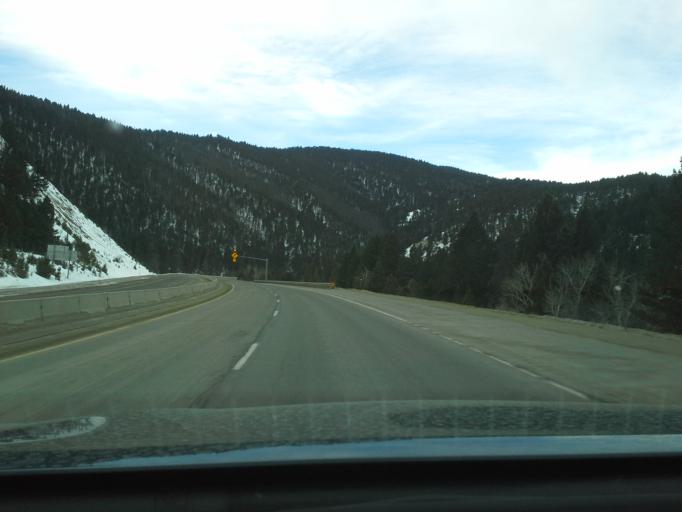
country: US
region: Montana
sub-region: Jefferson County
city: Boulder
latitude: 46.2611
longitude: -112.2070
